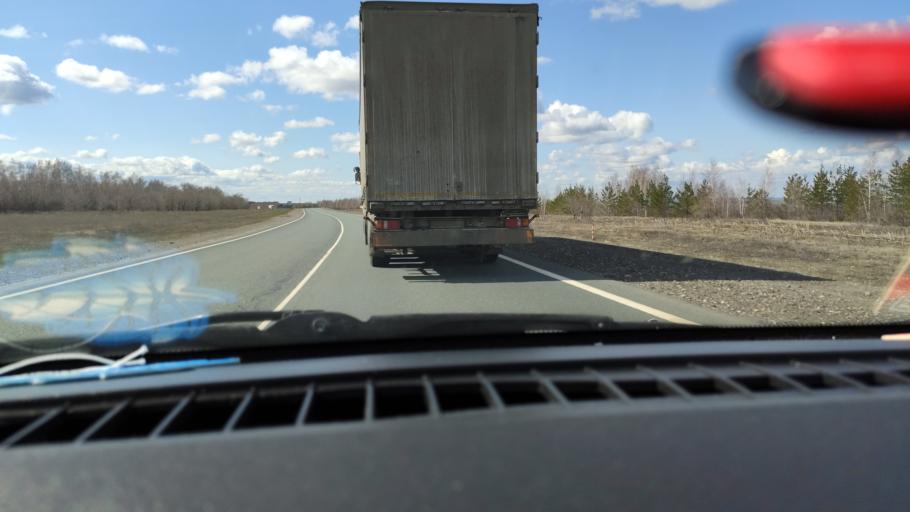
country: RU
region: Samara
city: Syzran'
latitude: 52.8585
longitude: 48.2622
